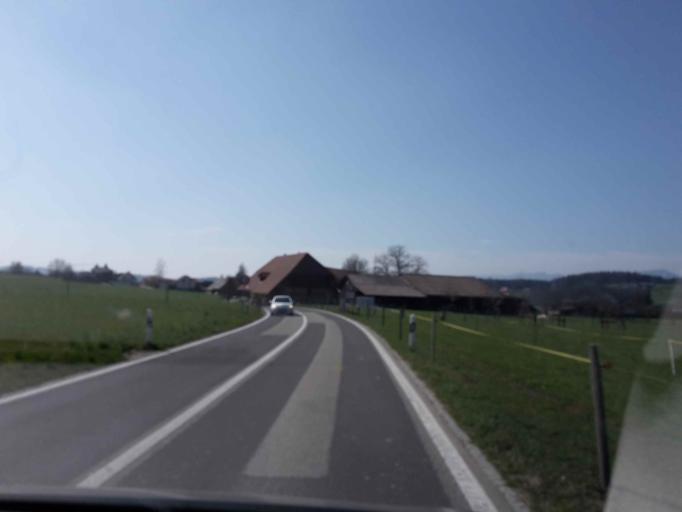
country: CH
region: Bern
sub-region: Oberaargau
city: Lotzwil
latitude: 47.1873
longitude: 7.7646
